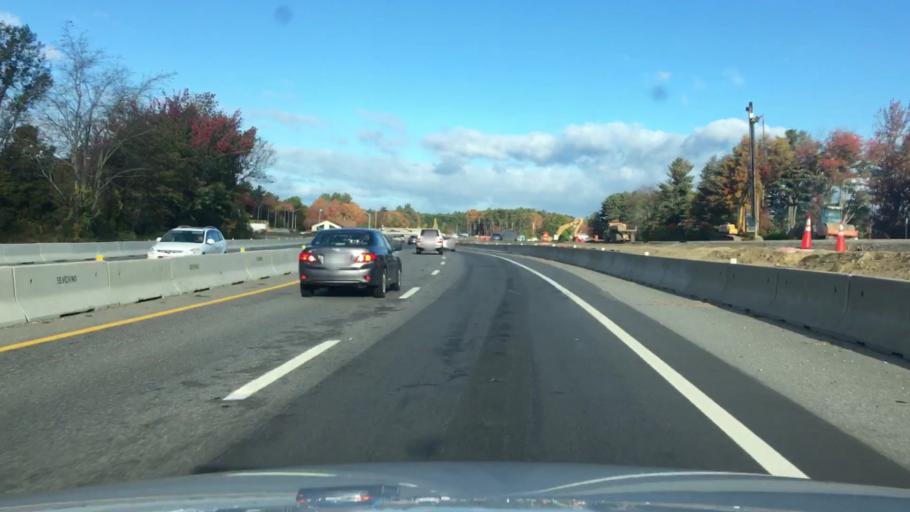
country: US
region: Maine
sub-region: York County
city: Eliot
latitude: 43.1235
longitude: -70.8319
